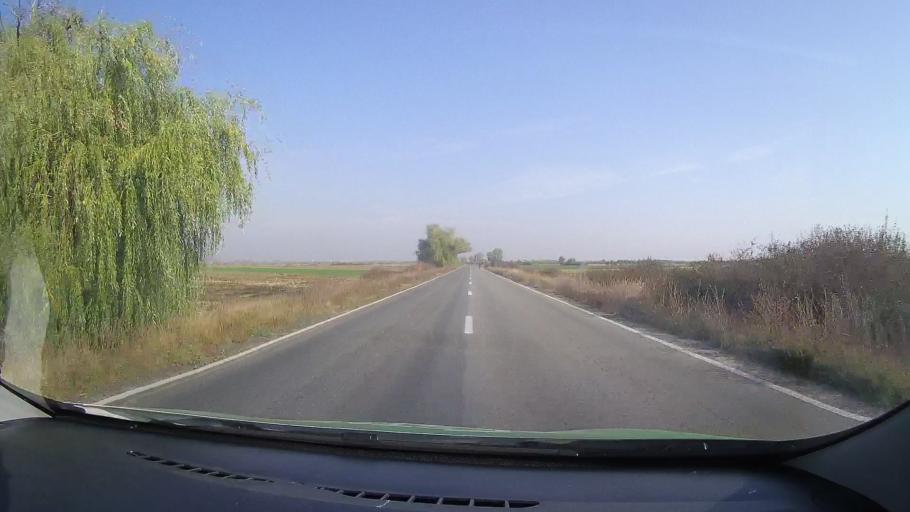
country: RO
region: Arad
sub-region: Comuna Pilu
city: Pilu
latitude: 46.5939
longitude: 21.3475
